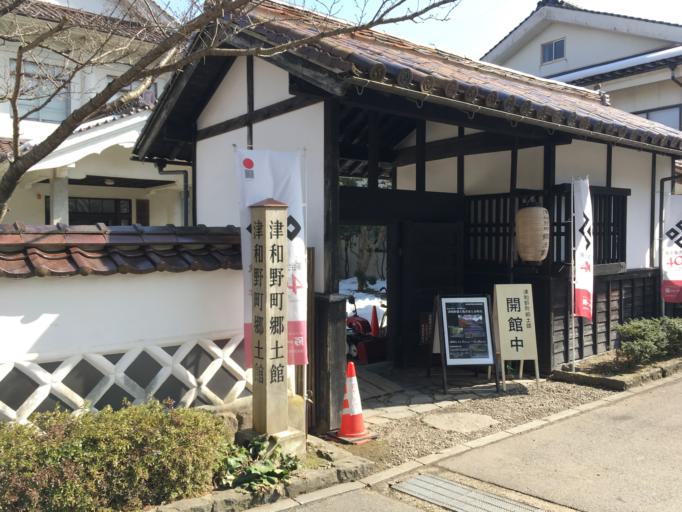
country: JP
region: Shimane
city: Masuda
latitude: 34.4656
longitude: 131.7730
